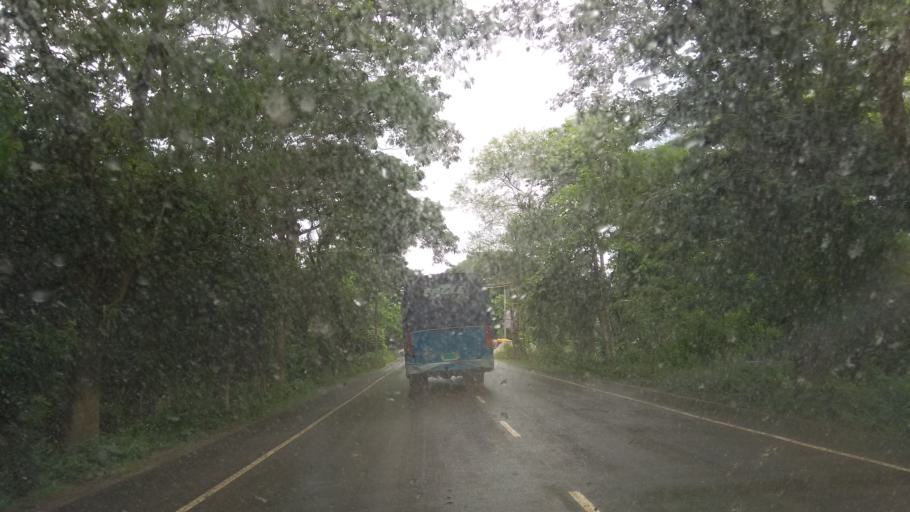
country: BD
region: Khulna
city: Kalia
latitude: 23.2506
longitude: 89.7589
